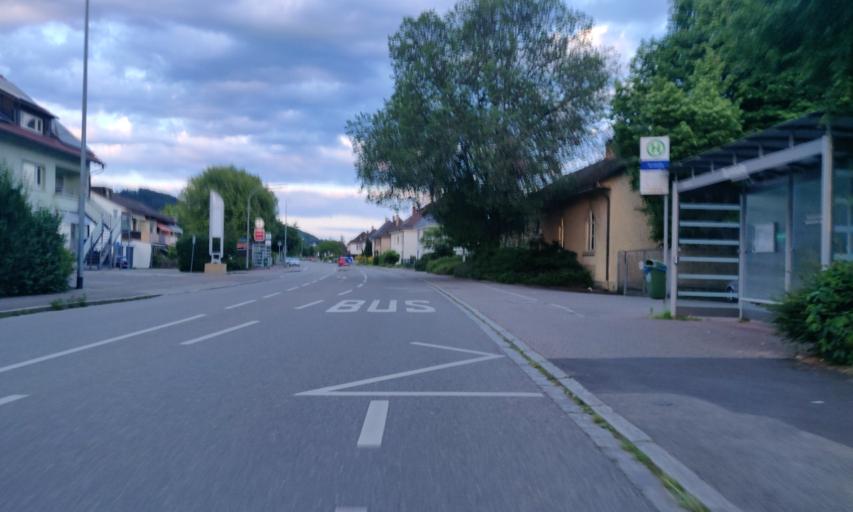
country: DE
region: Baden-Wuerttemberg
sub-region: Freiburg Region
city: Grenzach-Wyhlen
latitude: 47.5513
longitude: 7.6663
